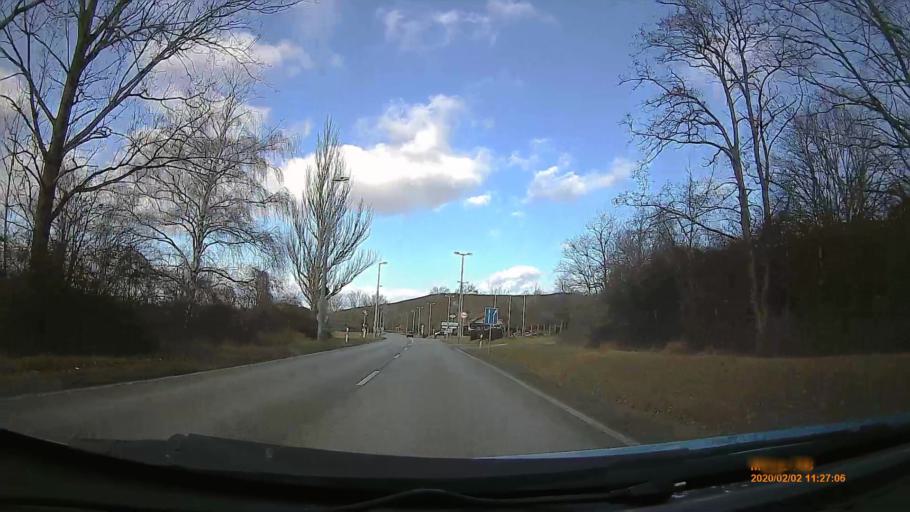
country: HU
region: Gyor-Moson-Sopron
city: Sopron
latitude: 47.7140
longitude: 16.5719
